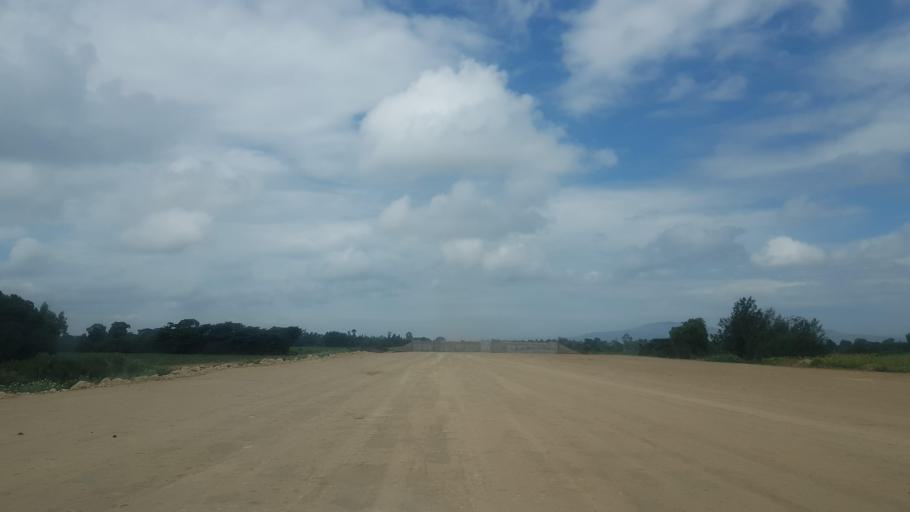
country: ET
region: Oromiya
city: Shashemene
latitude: 7.2447
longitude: 38.5855
